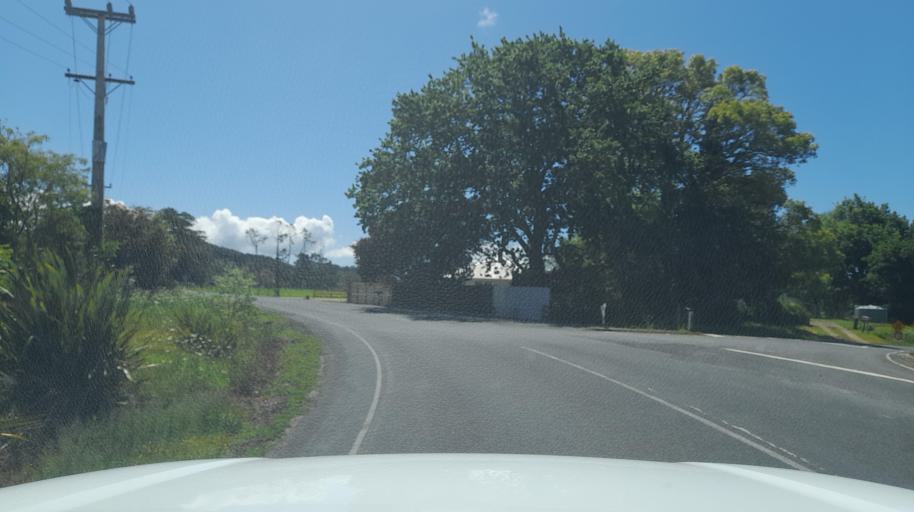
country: NZ
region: Northland
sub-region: Far North District
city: Taipa
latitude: -35.0431
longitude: 173.4965
